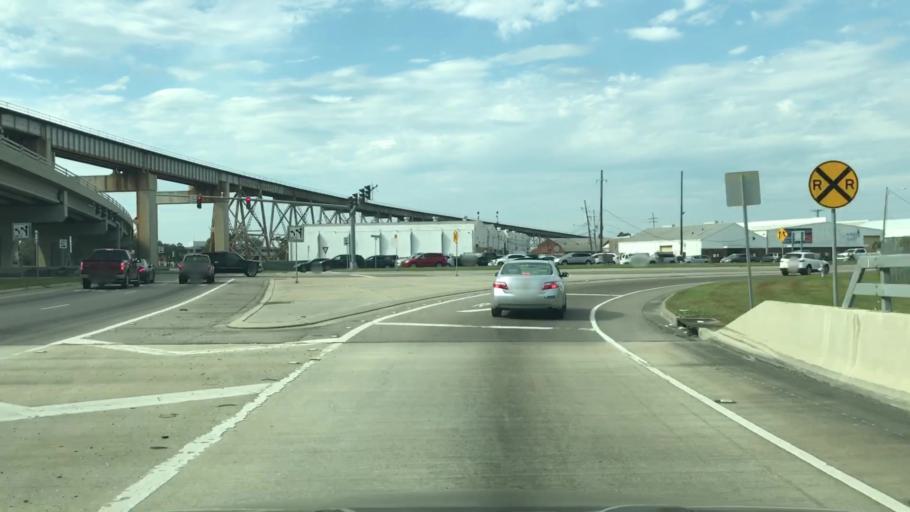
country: US
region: Louisiana
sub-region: Jefferson Parish
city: Elmwood
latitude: 29.9534
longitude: -90.1783
